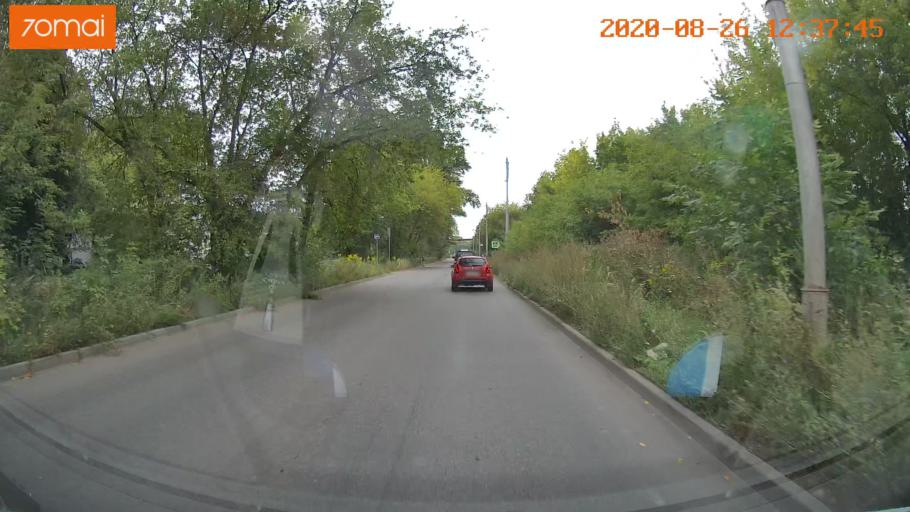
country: RU
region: Rjazan
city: Ryazan'
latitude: 54.6061
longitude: 39.7664
